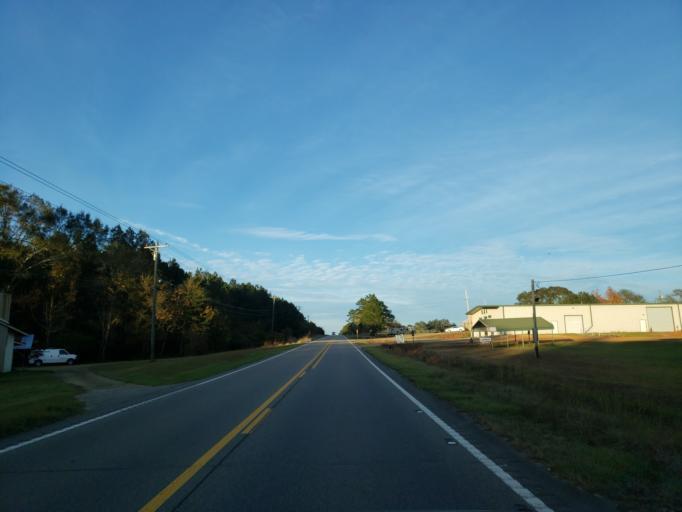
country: US
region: Mississippi
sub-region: Lamar County
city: Purvis
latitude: 31.1677
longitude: -89.3918
